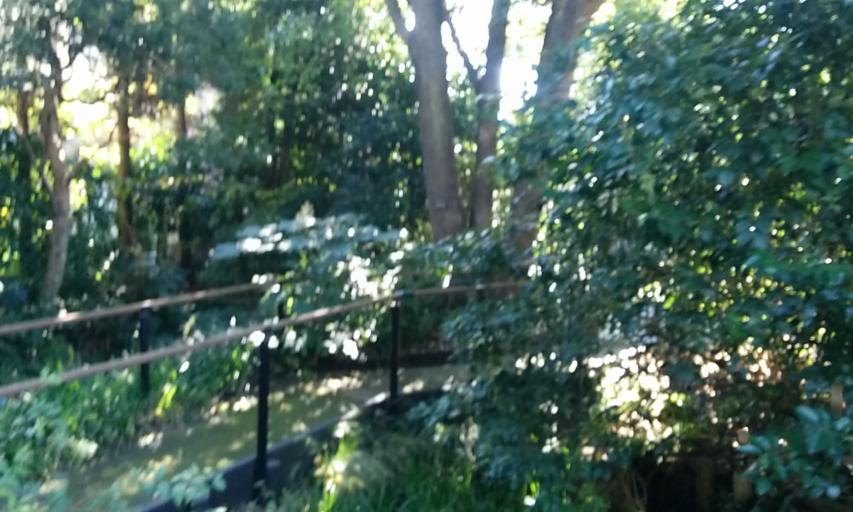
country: JP
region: Tokyo
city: Chofugaoka
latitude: 35.6571
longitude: 139.5813
